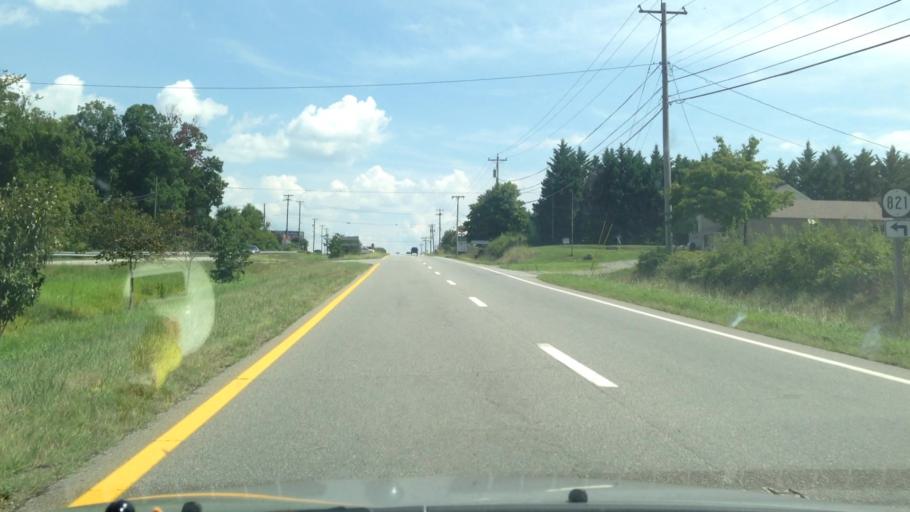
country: US
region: Virginia
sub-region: City of Martinsville
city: Martinsville
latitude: 36.6436
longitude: -79.8639
